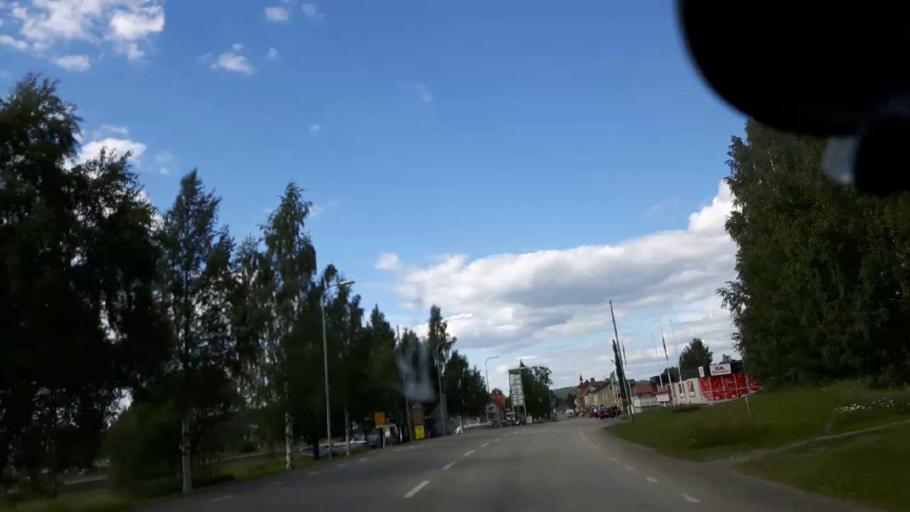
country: SE
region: Jaemtland
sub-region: Braecke Kommun
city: Braecke
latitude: 62.7487
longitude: 15.4194
